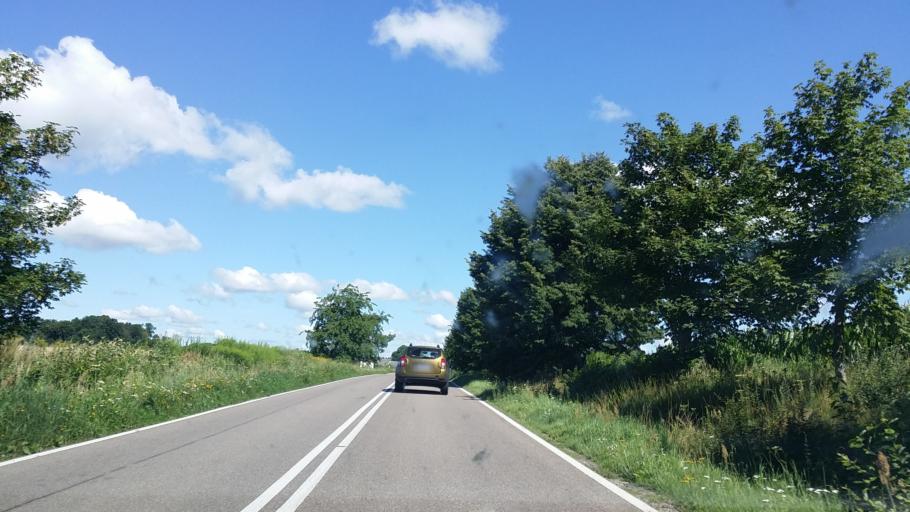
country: PL
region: West Pomeranian Voivodeship
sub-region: Powiat drawski
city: Kalisz Pomorski
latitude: 53.3317
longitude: 15.8952
